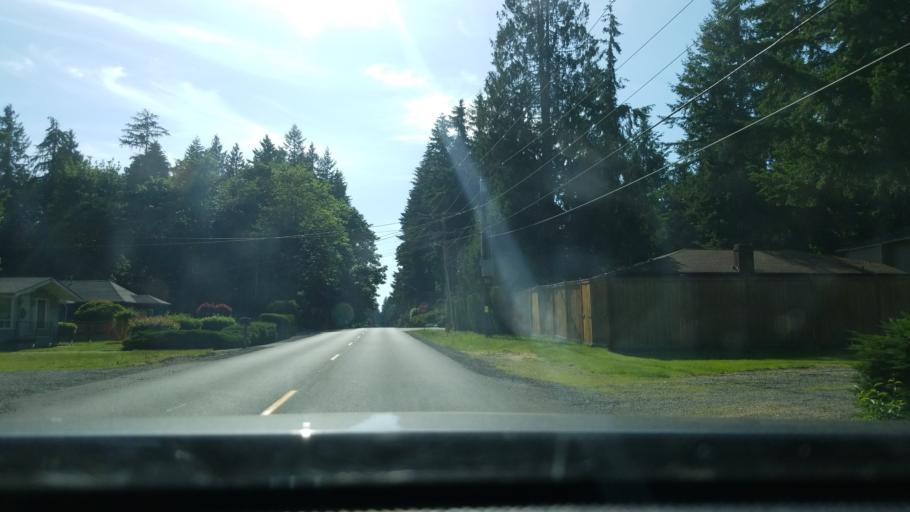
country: US
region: Washington
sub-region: King County
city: East Renton Highlands
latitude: 47.4757
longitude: -122.1364
